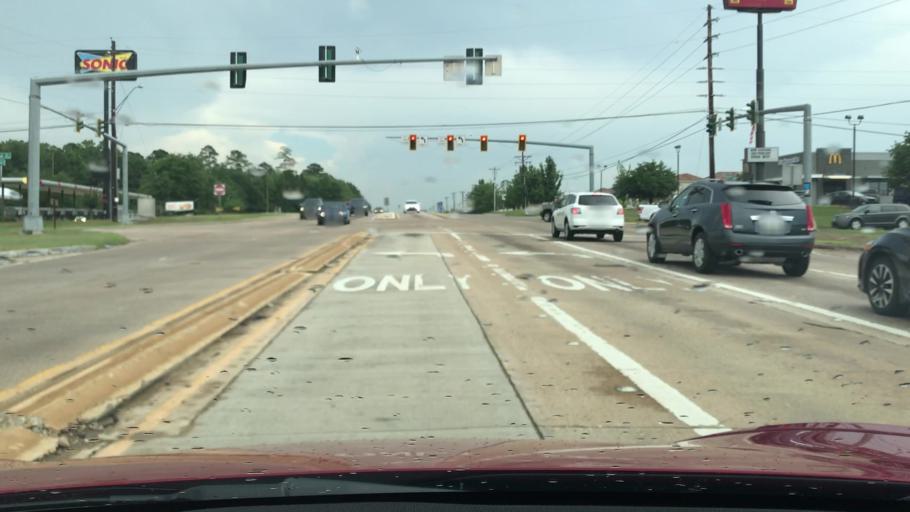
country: US
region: Louisiana
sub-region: Bossier Parish
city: Bossier City
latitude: 32.3983
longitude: -93.7639
